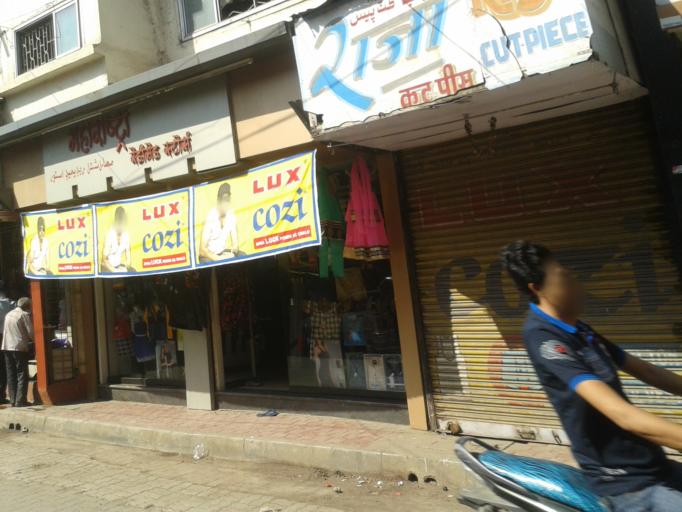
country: IN
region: Maharashtra
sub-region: Thane
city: Ulhasnagar
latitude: 19.2367
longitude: 73.1647
